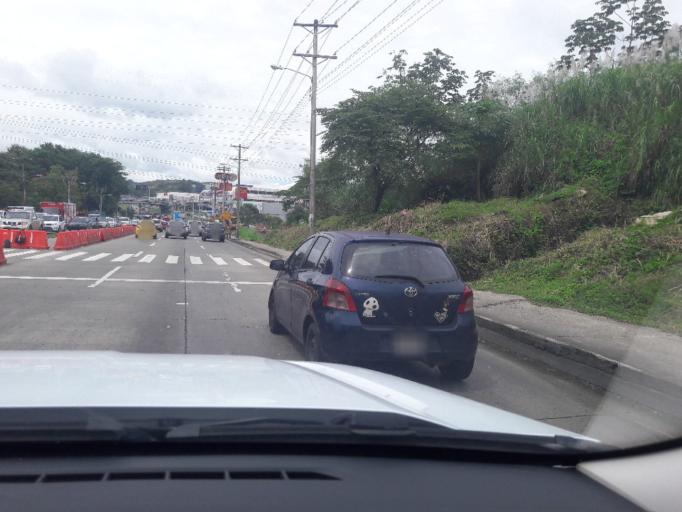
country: PA
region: Panama
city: Panama
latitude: 9.0263
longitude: -79.5291
